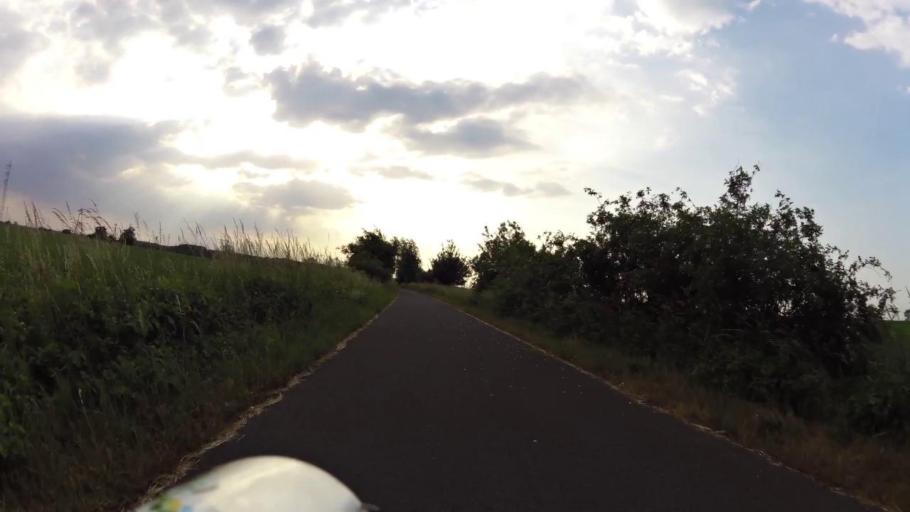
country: PL
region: Kujawsko-Pomorskie
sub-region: Powiat chelminski
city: Unislaw
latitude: 53.1801
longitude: 18.4061
